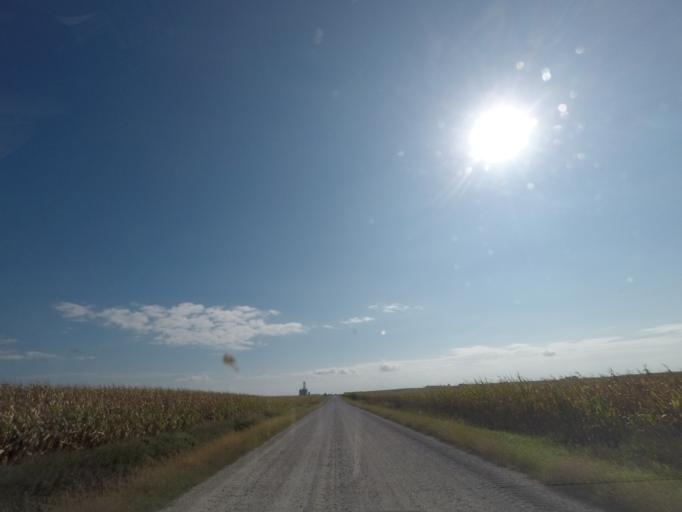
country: US
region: Iowa
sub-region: Story County
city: Nevada
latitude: 42.0490
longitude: -93.4242
